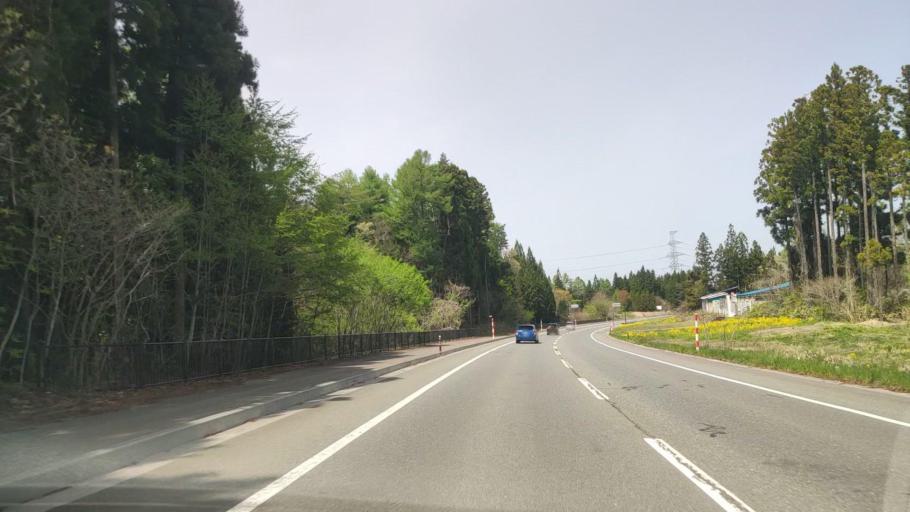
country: JP
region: Aomori
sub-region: Misawa Shi
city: Inuotose
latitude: 40.6792
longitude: 141.1718
